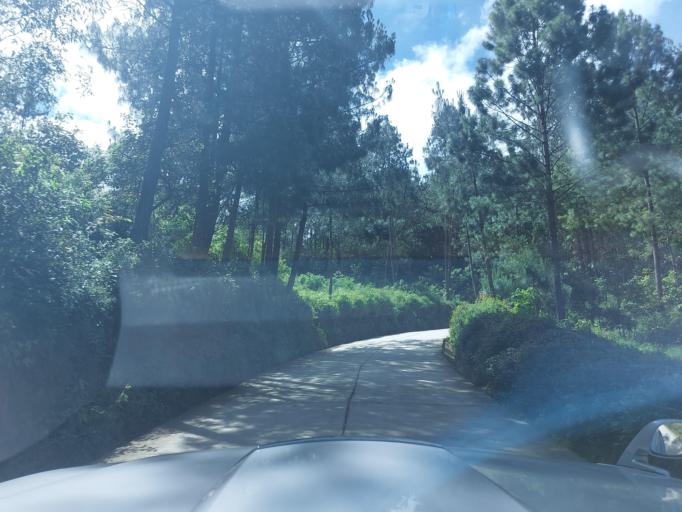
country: GT
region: Chimaltenango
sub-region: Municipio de San Juan Comalapa
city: Comalapa
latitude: 14.7529
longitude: -90.8675
